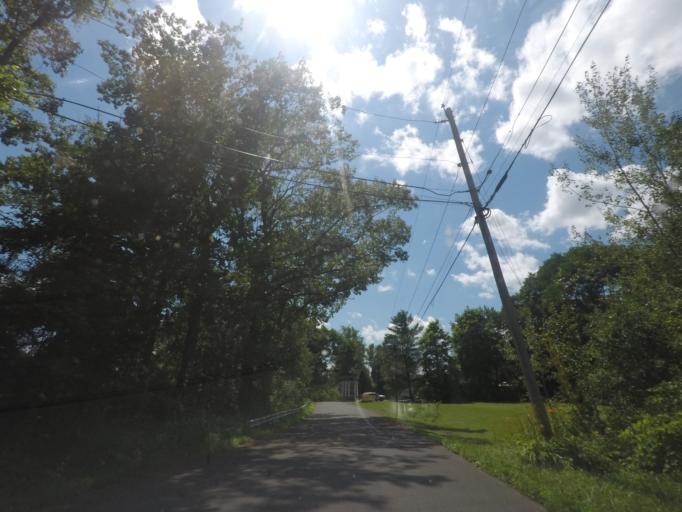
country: US
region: New York
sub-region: Albany County
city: Voorheesville
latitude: 42.7188
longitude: -73.9489
